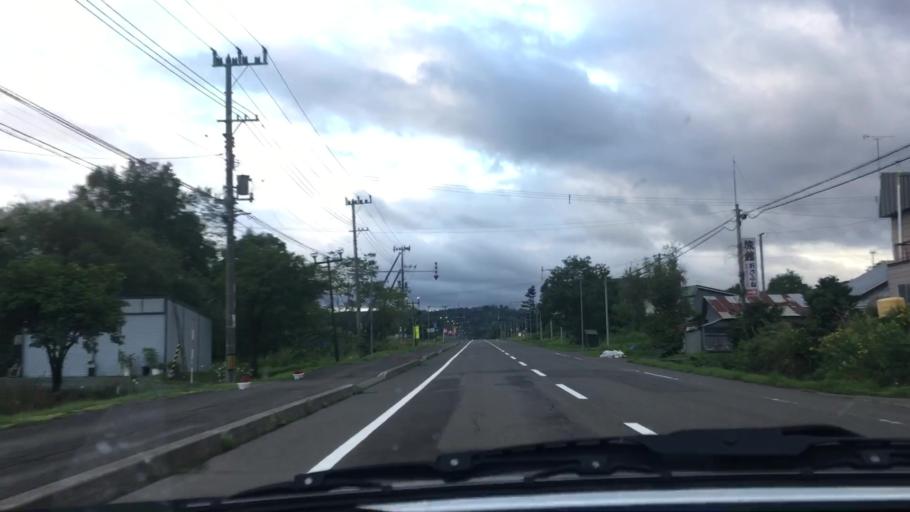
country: JP
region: Hokkaido
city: Shimo-furano
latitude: 42.9939
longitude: 142.4020
